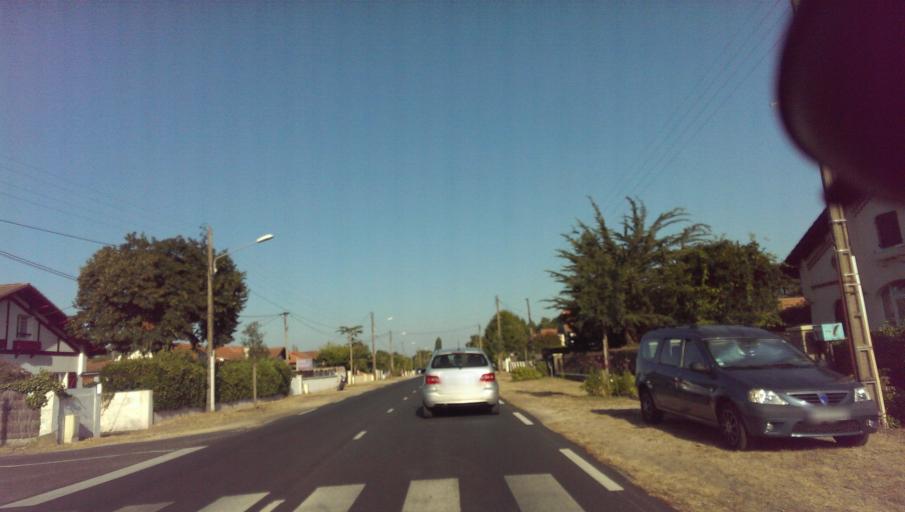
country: FR
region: Aquitaine
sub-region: Departement des Landes
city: Mimizan
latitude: 44.2111
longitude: -1.2596
